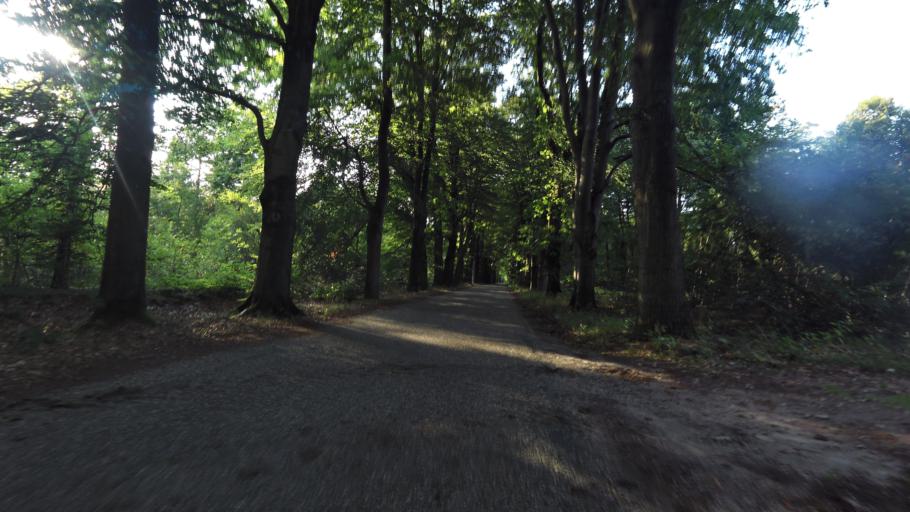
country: NL
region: Gelderland
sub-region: Gemeente Renkum
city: Oosterbeek
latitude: 52.0177
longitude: 5.8476
